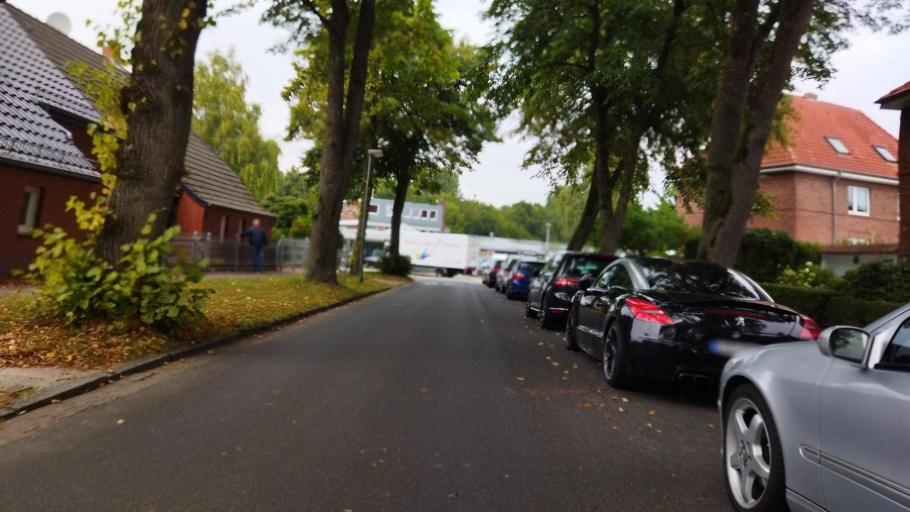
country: DE
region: Lower Saxony
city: Leer
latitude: 53.2374
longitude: 7.4434
